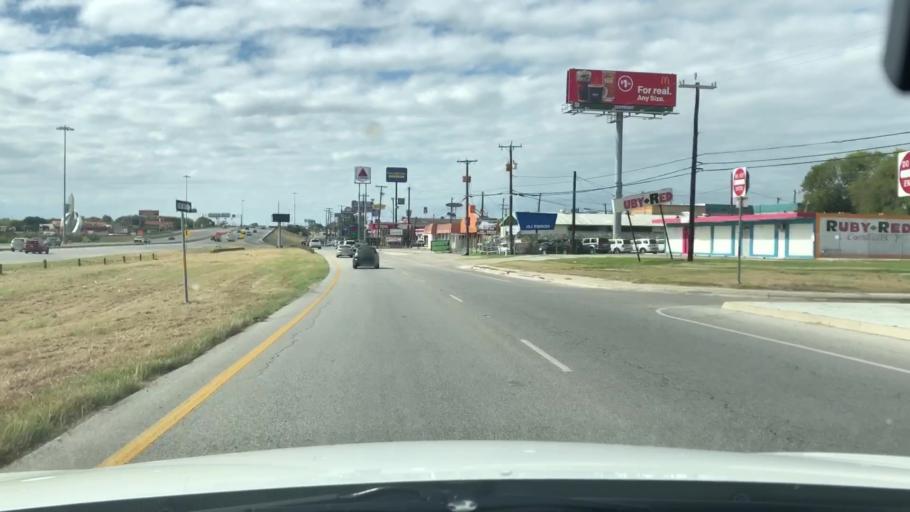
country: US
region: Texas
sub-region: Bexar County
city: Lackland Air Force Base
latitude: 29.4041
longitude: -98.6223
